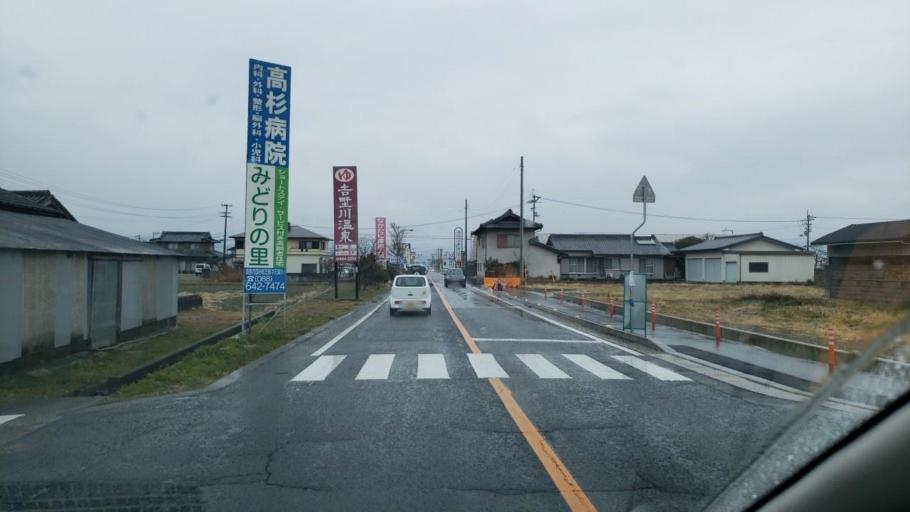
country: JP
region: Tokushima
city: Ishii
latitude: 34.1103
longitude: 134.4367
